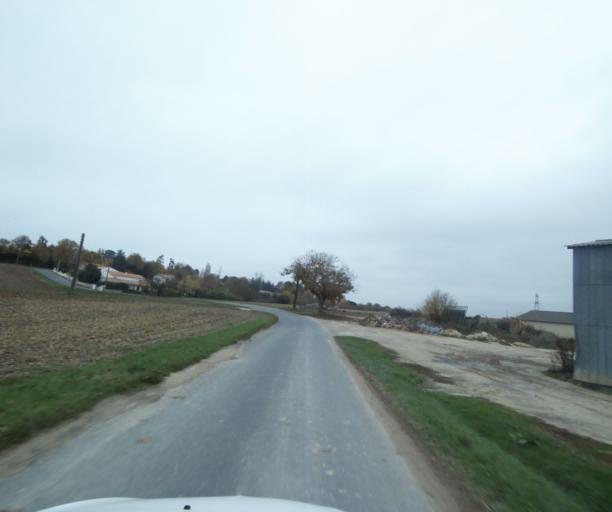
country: FR
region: Poitou-Charentes
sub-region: Departement de la Charente-Maritime
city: Fontcouverte
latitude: 45.7395
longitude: -0.5966
